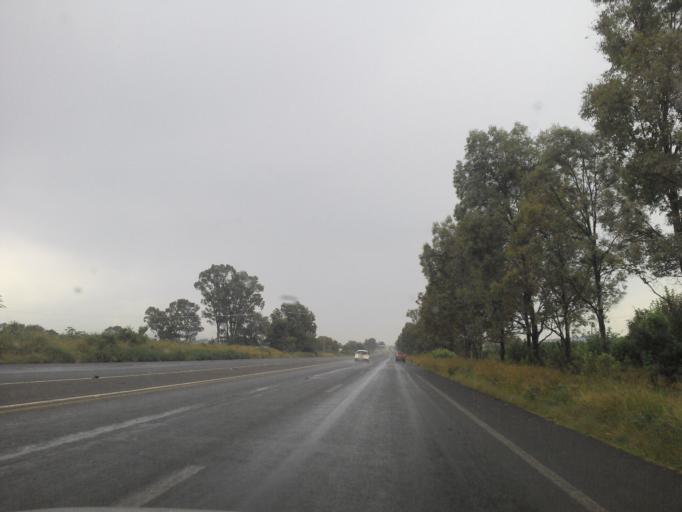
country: MX
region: Jalisco
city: Tepatitlan de Morelos
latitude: 20.8808
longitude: -102.6936
